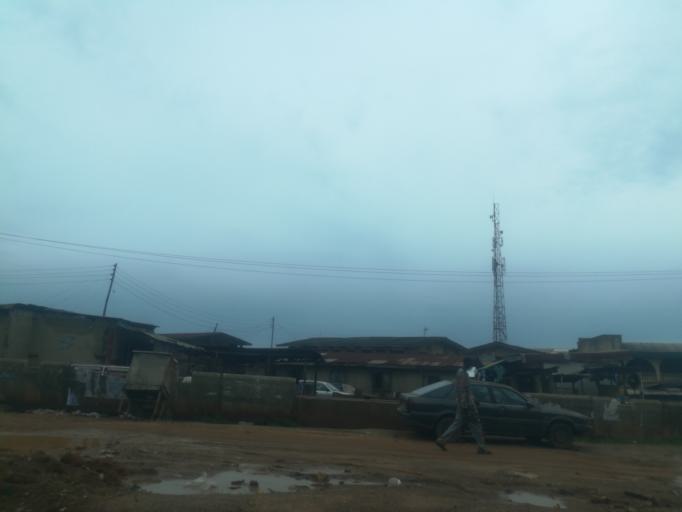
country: NG
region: Oyo
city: Ibadan
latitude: 7.3921
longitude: 3.9594
